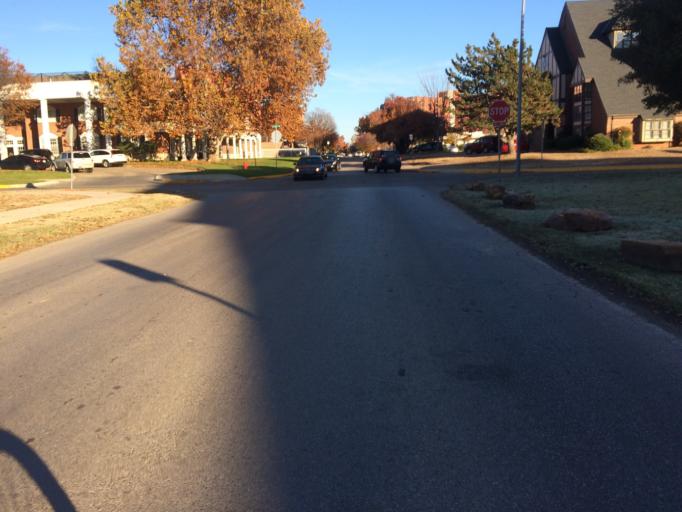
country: US
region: Oklahoma
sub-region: Cleveland County
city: Norman
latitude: 35.2009
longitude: -97.4494
